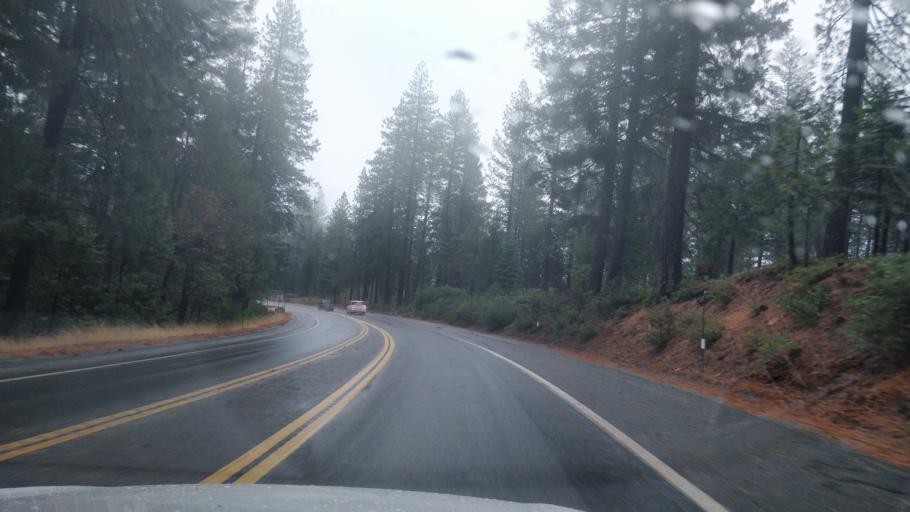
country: US
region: California
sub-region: Nevada County
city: Nevada City
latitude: 39.3200
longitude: -120.8441
